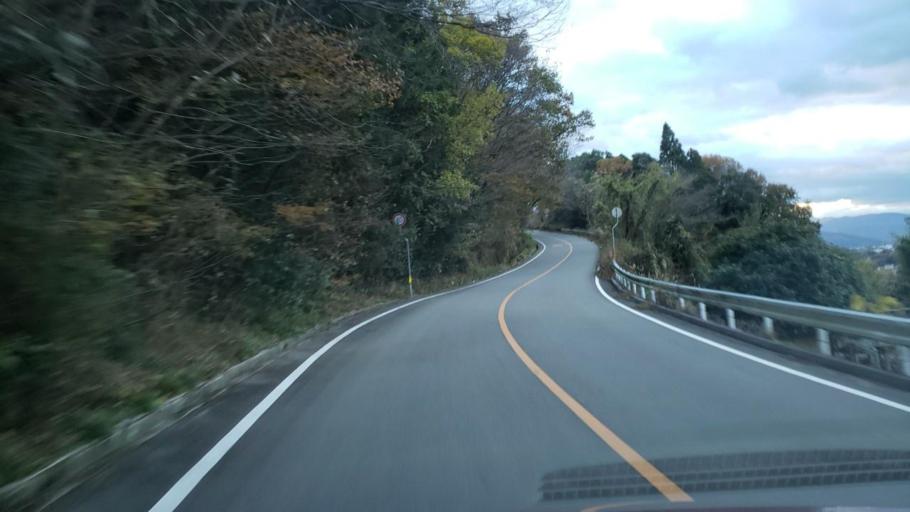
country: JP
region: Tokushima
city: Wakimachi
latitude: 34.0862
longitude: 134.1790
